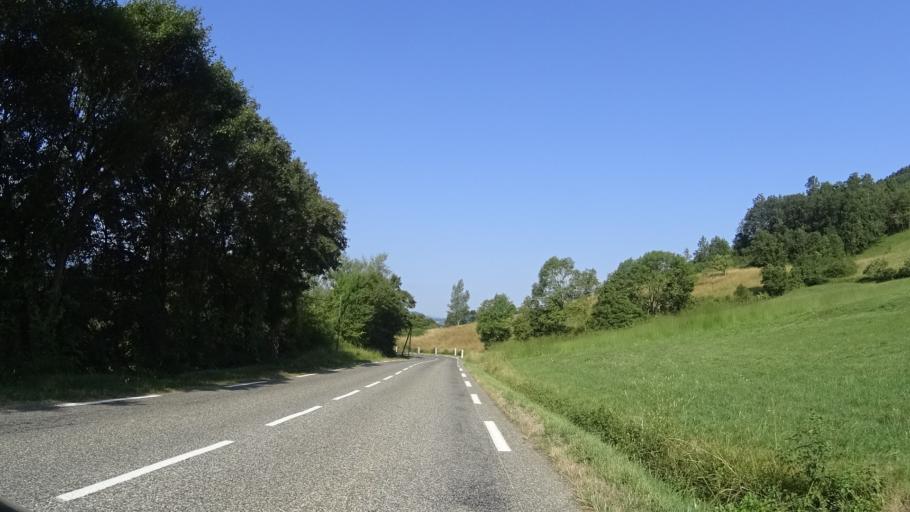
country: FR
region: Midi-Pyrenees
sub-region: Departement de l'Ariege
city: Belesta
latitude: 42.9107
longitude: 1.9471
